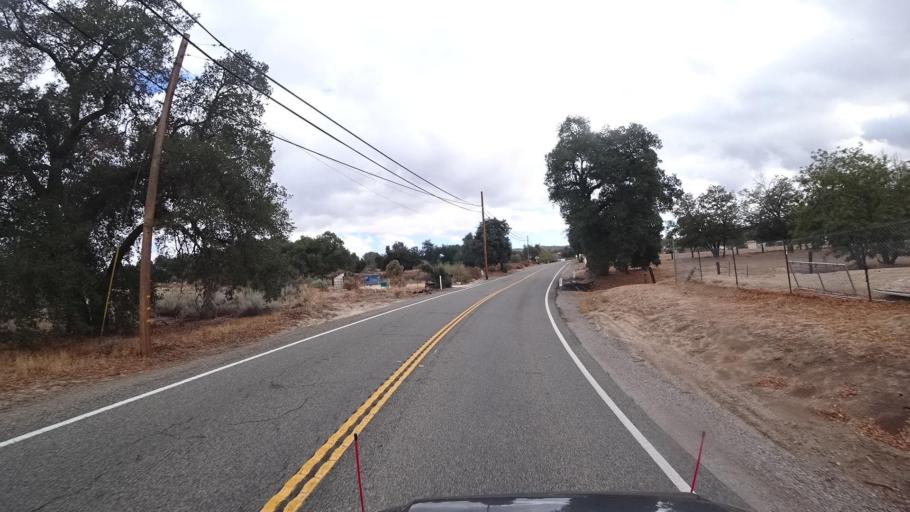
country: US
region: California
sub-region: San Diego County
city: Campo
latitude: 32.6395
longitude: -116.4315
